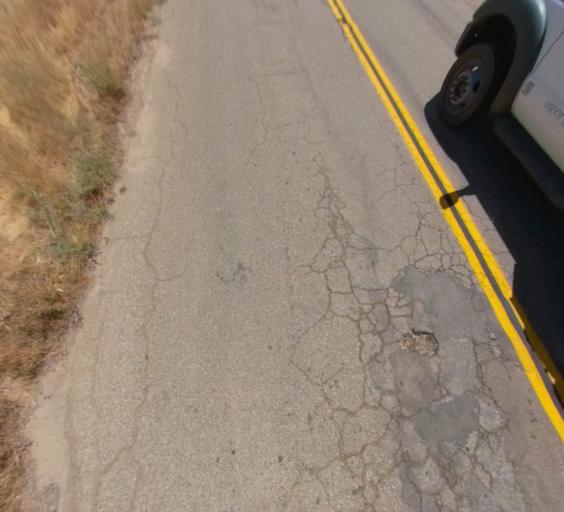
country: US
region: California
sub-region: Madera County
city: Bonadelle Ranchos-Madera Ranchos
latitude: 36.8946
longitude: -119.8210
